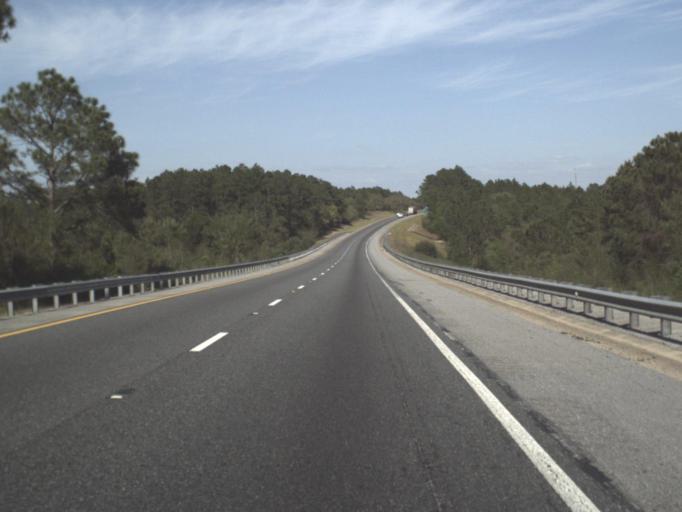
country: US
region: Florida
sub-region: Okaloosa County
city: Crestview
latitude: 30.7214
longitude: -86.5952
